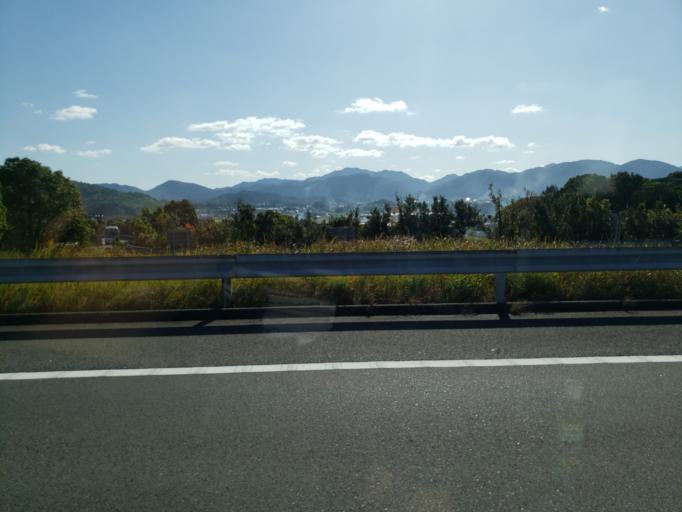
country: JP
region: Hyogo
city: Sumoto
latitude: 34.3421
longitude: 134.8404
